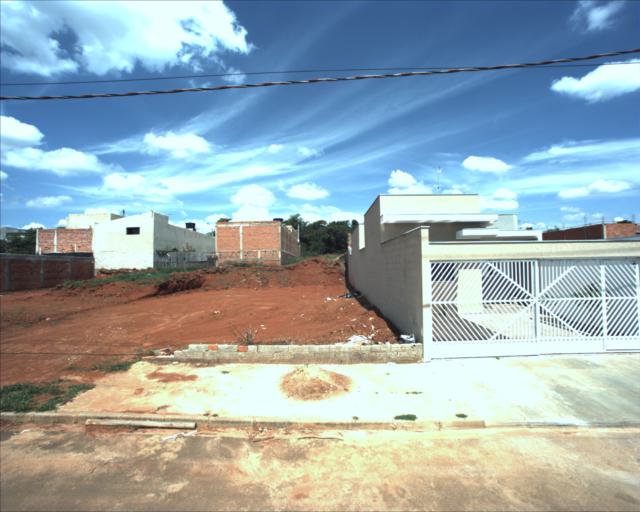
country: BR
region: Sao Paulo
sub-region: Sorocaba
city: Sorocaba
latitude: -23.4103
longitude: -47.4115
